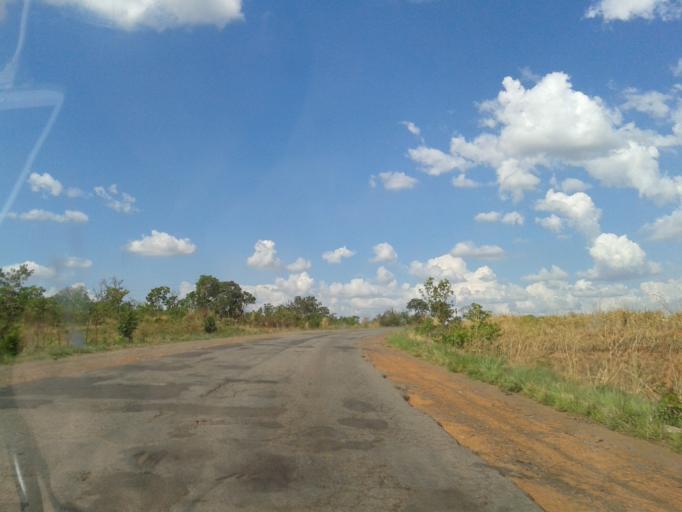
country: BR
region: Goias
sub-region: Caldas Novas
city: Caldas Novas
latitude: -17.7000
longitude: -48.7263
